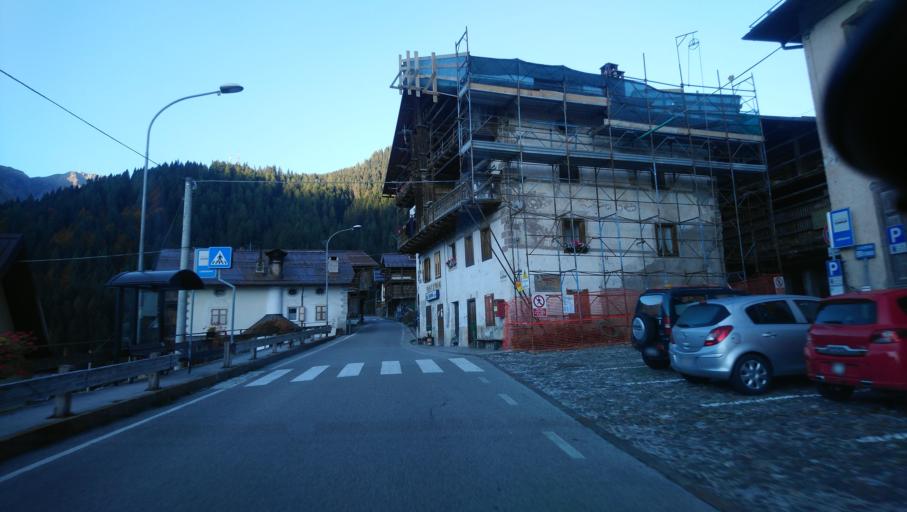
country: IT
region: Veneto
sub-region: Provincia di Belluno
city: Falcade Alto
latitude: 46.3554
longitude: 11.8586
